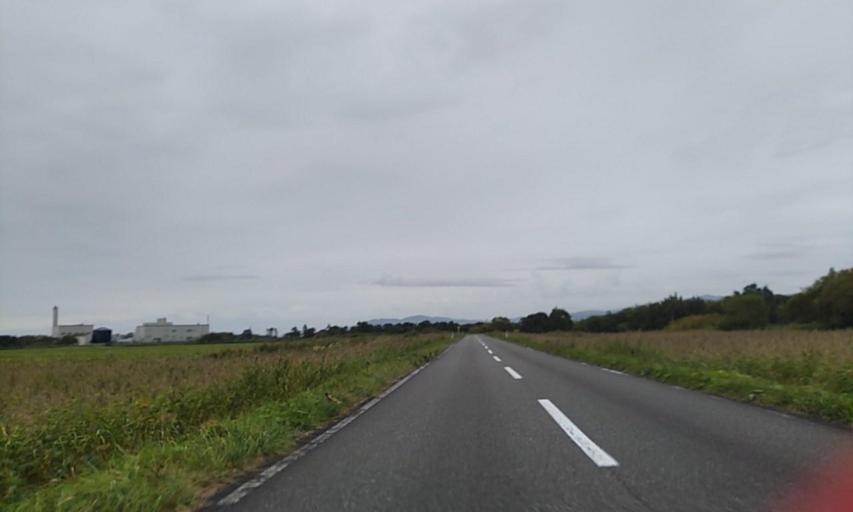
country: JP
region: Hokkaido
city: Makubetsu
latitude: 45.1526
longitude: 142.3401
